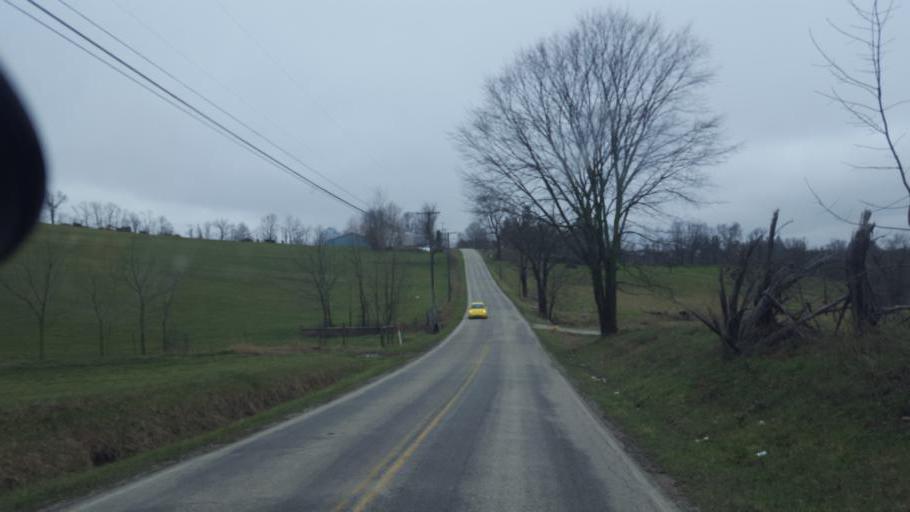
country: US
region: Ohio
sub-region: Richland County
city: Lexington
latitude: 40.6866
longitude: -82.5365
